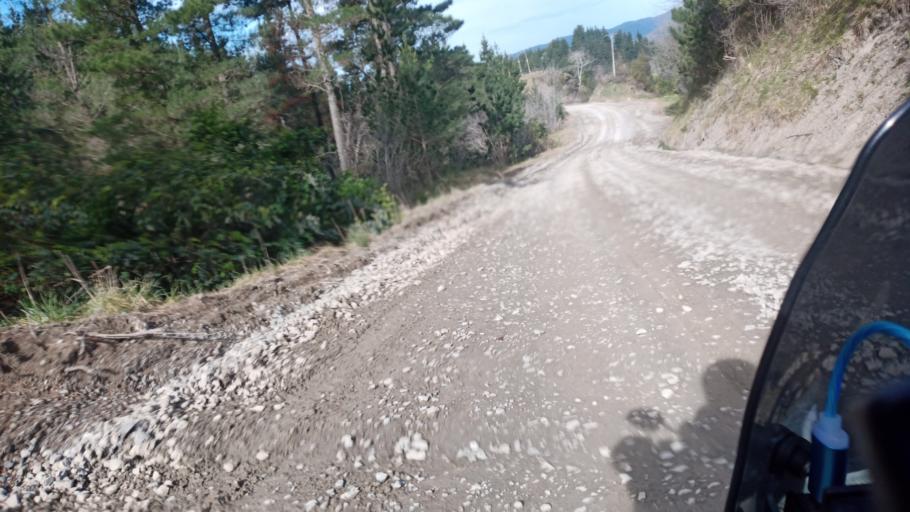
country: NZ
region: Gisborne
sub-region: Gisborne District
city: Gisborne
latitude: -38.1206
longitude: 178.1513
